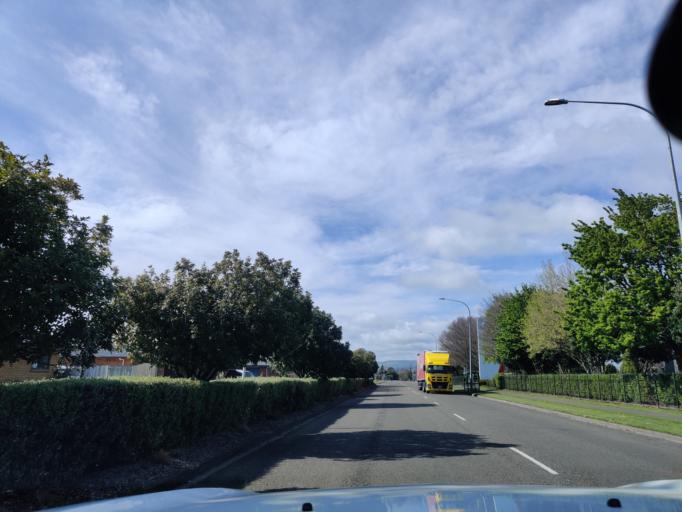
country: NZ
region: Manawatu-Wanganui
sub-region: Palmerston North City
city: Palmerston North
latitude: -40.3323
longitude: 175.6536
